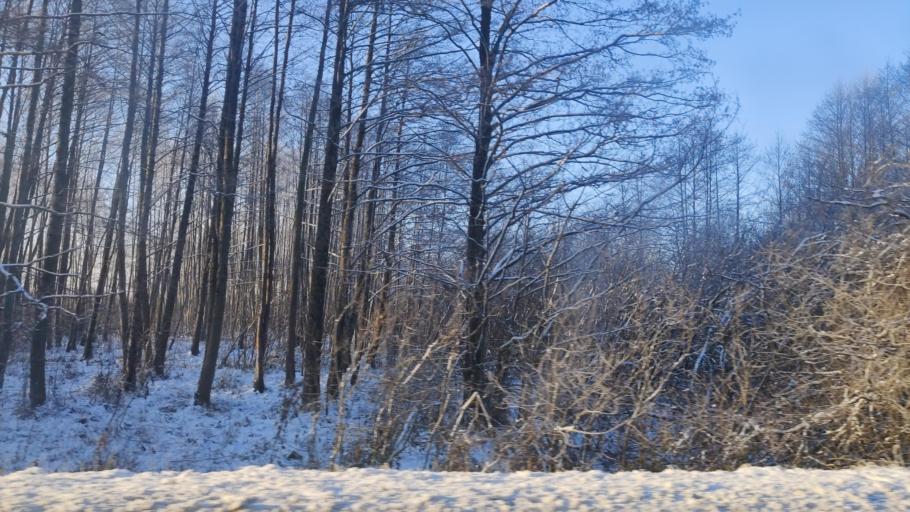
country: PL
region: Kujawsko-Pomorskie
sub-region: Powiat zninski
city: Barcin
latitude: 52.8738
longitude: 17.8987
